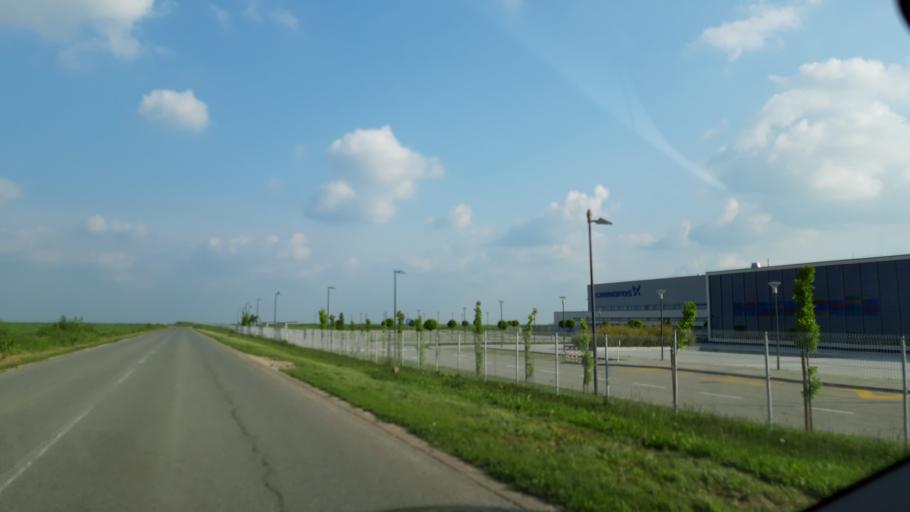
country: RS
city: Beska
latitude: 45.0942
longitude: 20.0953
